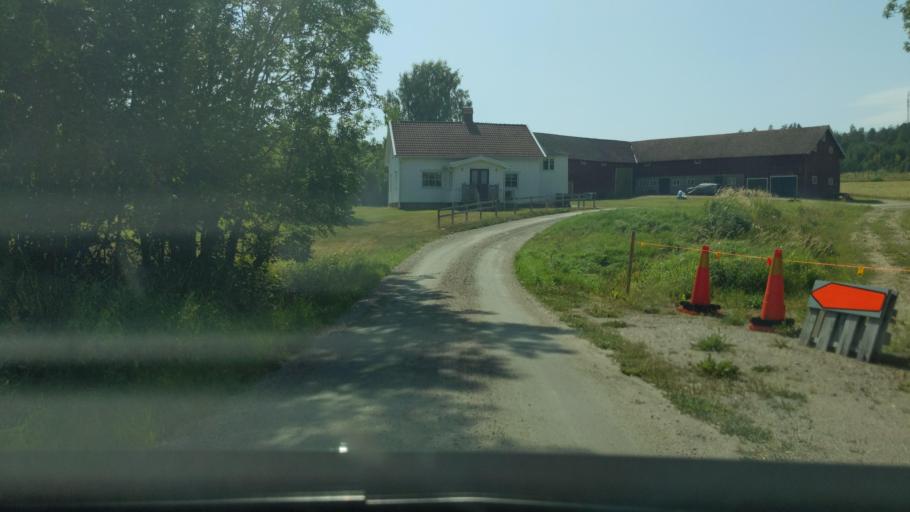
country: SE
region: Vaestra Goetaland
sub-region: Uddevalla Kommun
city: Uddevalla
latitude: 58.3354
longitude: 11.8026
